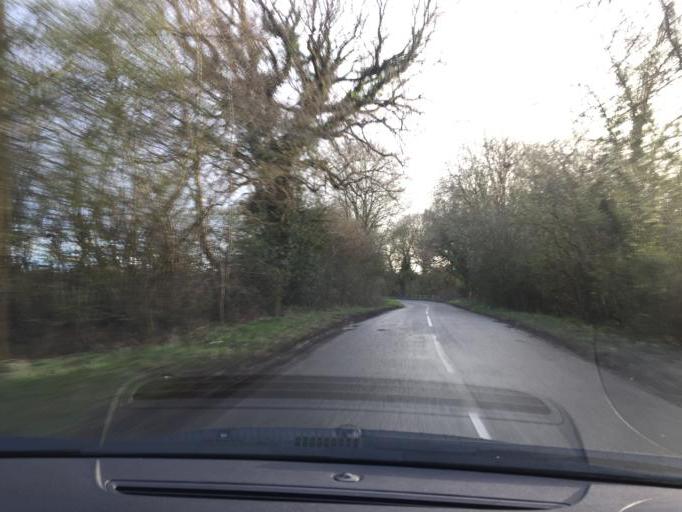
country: GB
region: England
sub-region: Warwickshire
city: Wroxall
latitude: 52.2752
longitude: -1.6931
